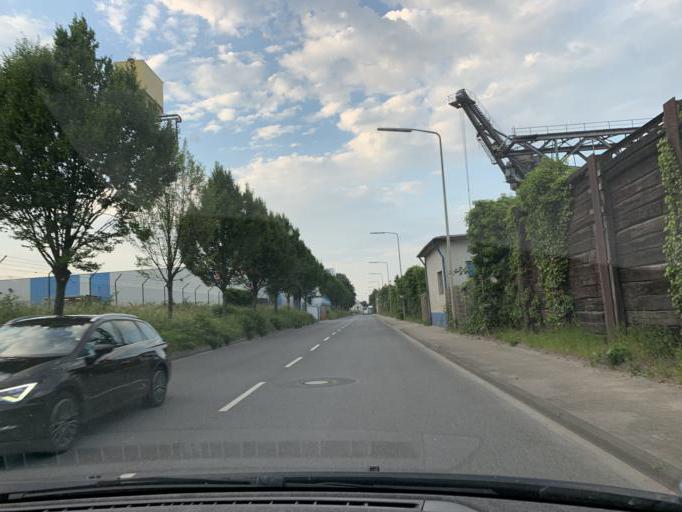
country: DE
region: North Rhine-Westphalia
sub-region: Regierungsbezirk Dusseldorf
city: Dusseldorf
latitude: 51.2172
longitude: 6.7408
